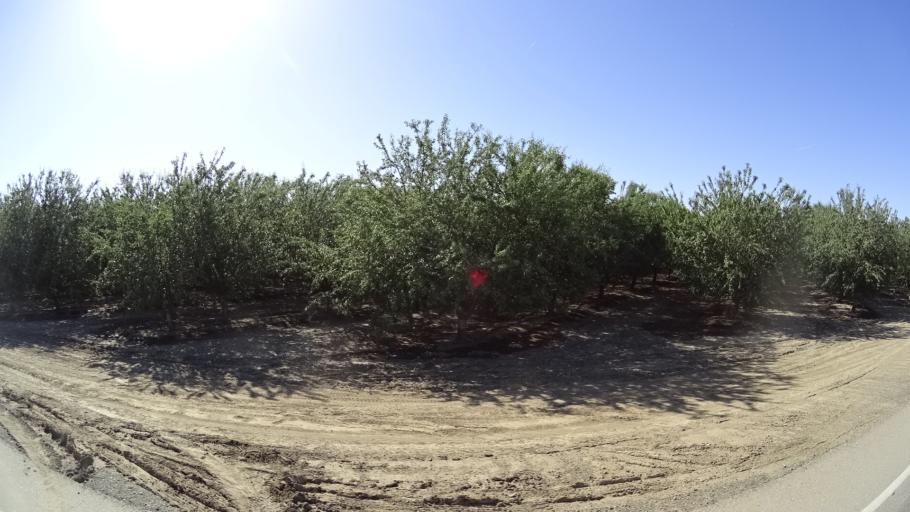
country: US
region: California
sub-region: Fresno County
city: Huron
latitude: 36.1324
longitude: -120.0182
